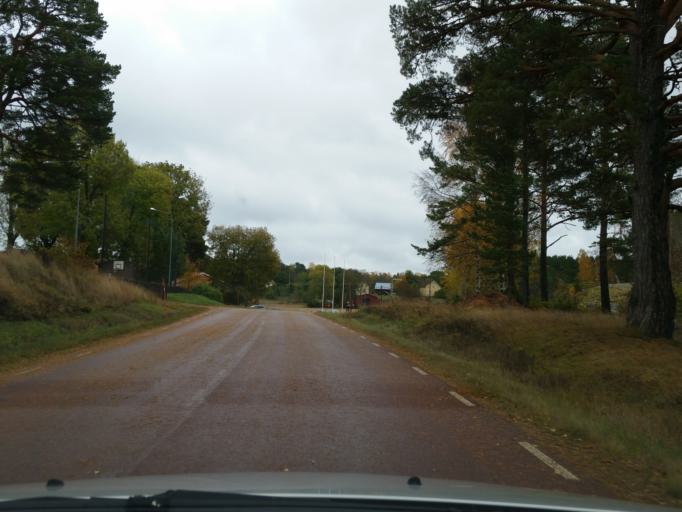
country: AX
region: Alands landsbygd
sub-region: Lumparland
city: Lumparland
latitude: 60.1172
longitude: 20.2560
